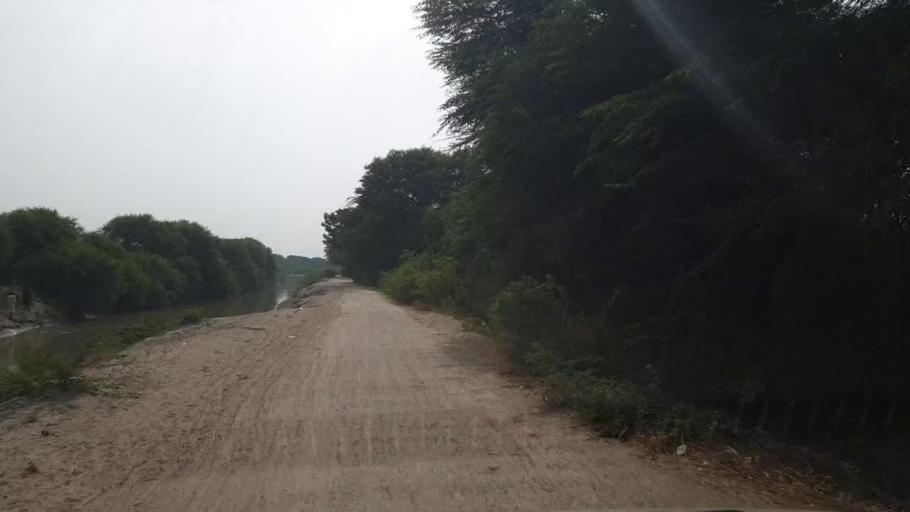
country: PK
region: Sindh
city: Matli
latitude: 25.0072
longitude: 68.7012
